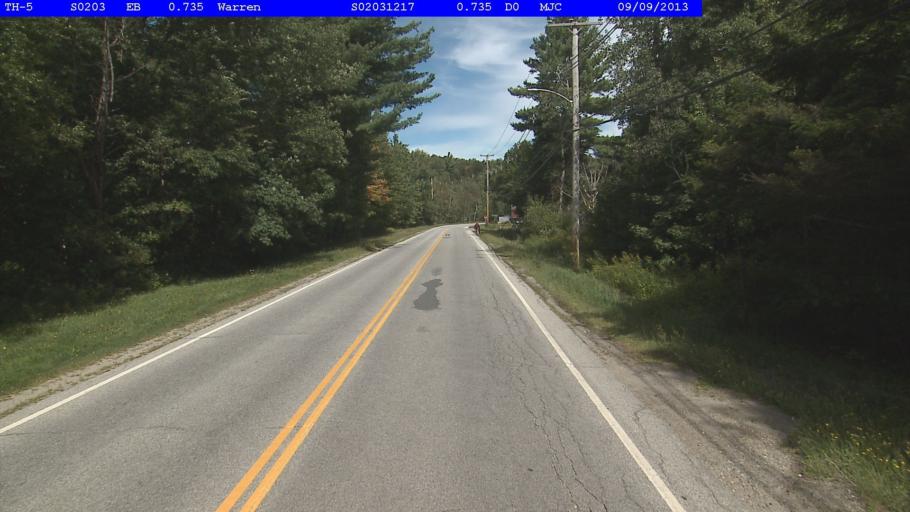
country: US
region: Vermont
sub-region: Addison County
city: Bristol
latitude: 44.1413
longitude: -72.8845
